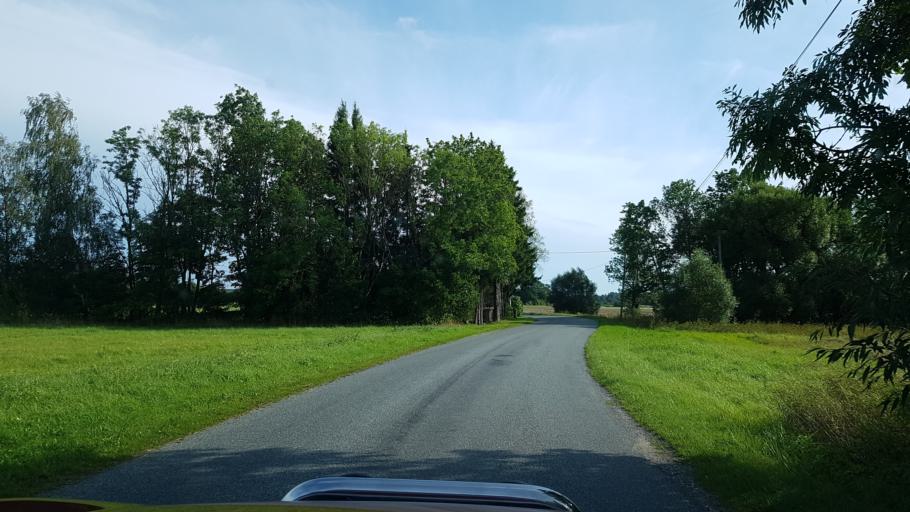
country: EE
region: Laeaene
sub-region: Lihula vald
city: Lihula
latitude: 58.4448
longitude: 24.0026
